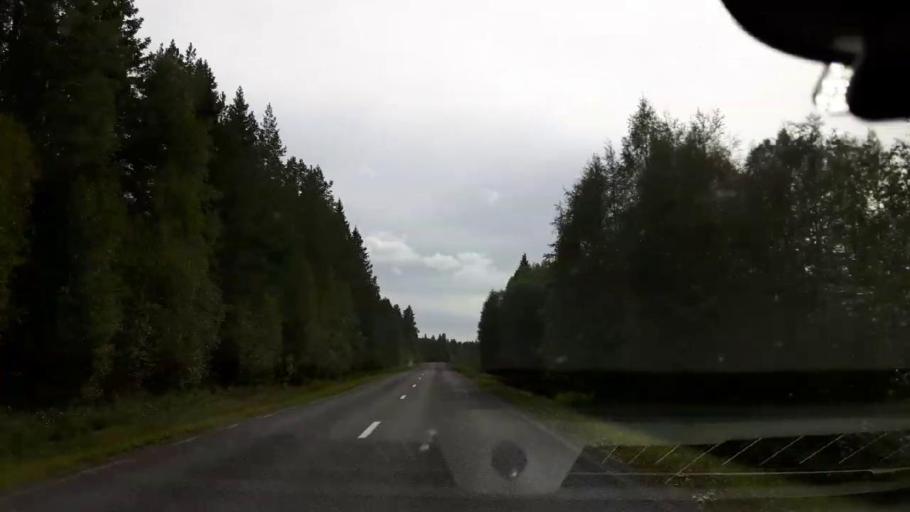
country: SE
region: Jaemtland
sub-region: Ragunda Kommun
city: Hammarstrand
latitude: 63.1155
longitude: 15.9058
